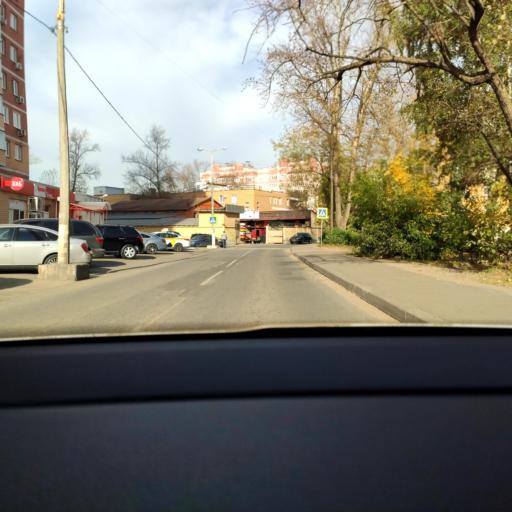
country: RU
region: Moskovskaya
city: Ivanteyevka
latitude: 55.9700
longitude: 37.9320
